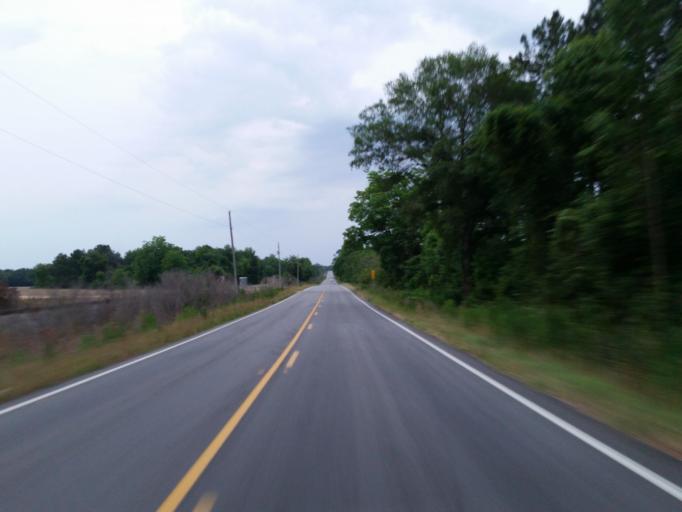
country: US
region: Georgia
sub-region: Turner County
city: Ashburn
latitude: 31.8157
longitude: -83.7251
